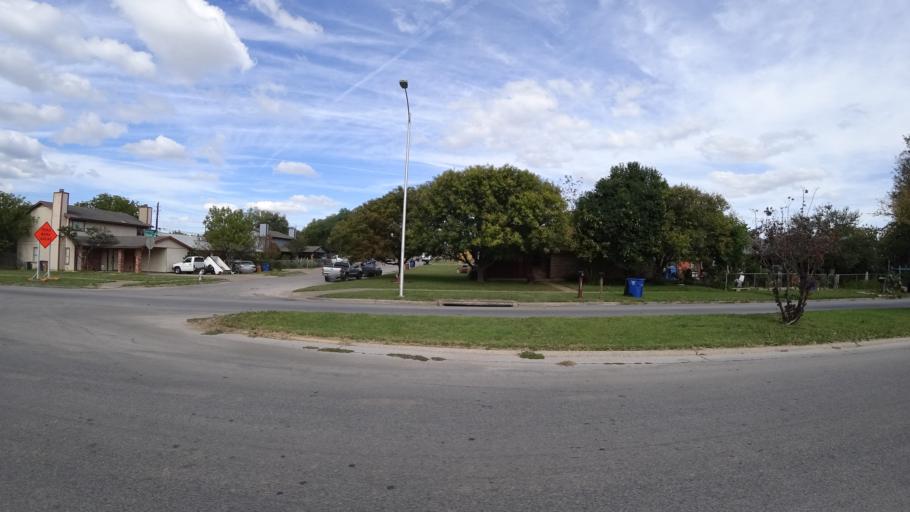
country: US
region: Texas
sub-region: Travis County
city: Onion Creek
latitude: 30.1959
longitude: -97.7592
